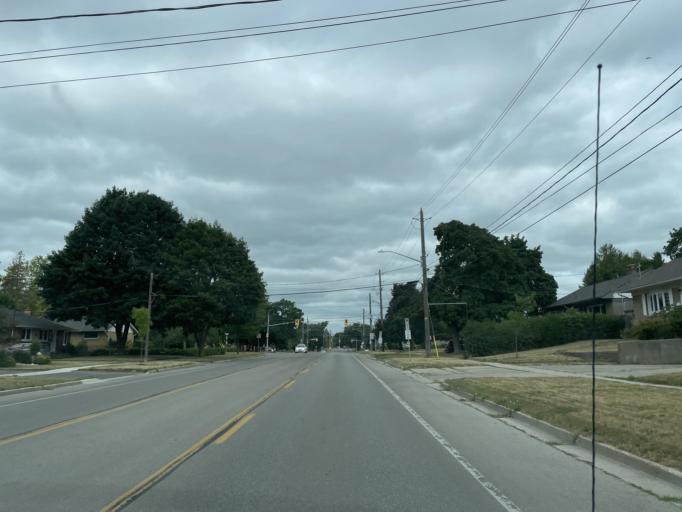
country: CA
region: Ontario
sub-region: Wellington County
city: Guelph
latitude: 43.5644
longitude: -80.2555
